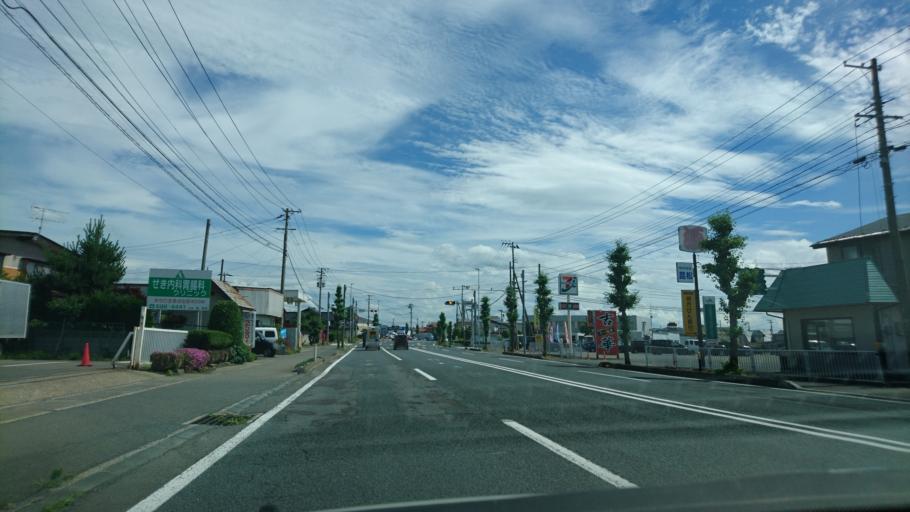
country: JP
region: Iwate
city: Morioka-shi
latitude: 39.6282
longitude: 141.1745
